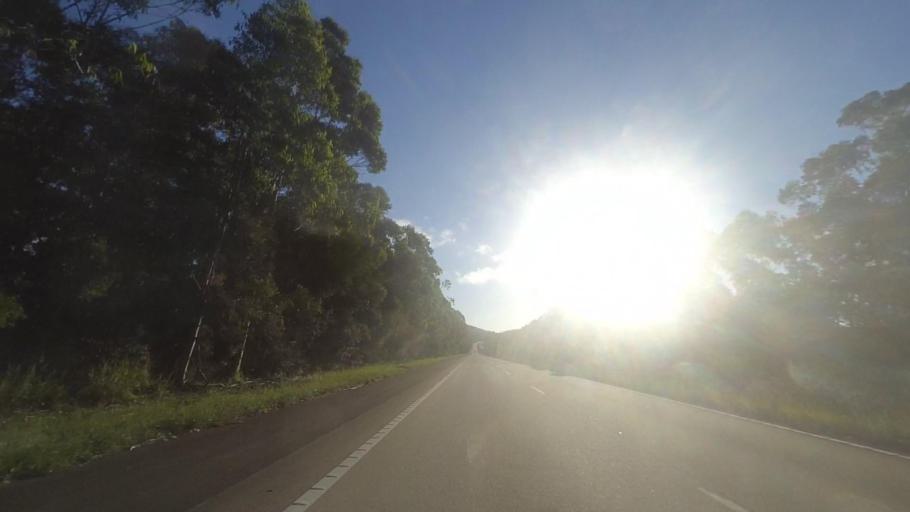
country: AU
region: New South Wales
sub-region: Great Lakes
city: Bulahdelah
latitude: -32.3790
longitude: 152.2714
